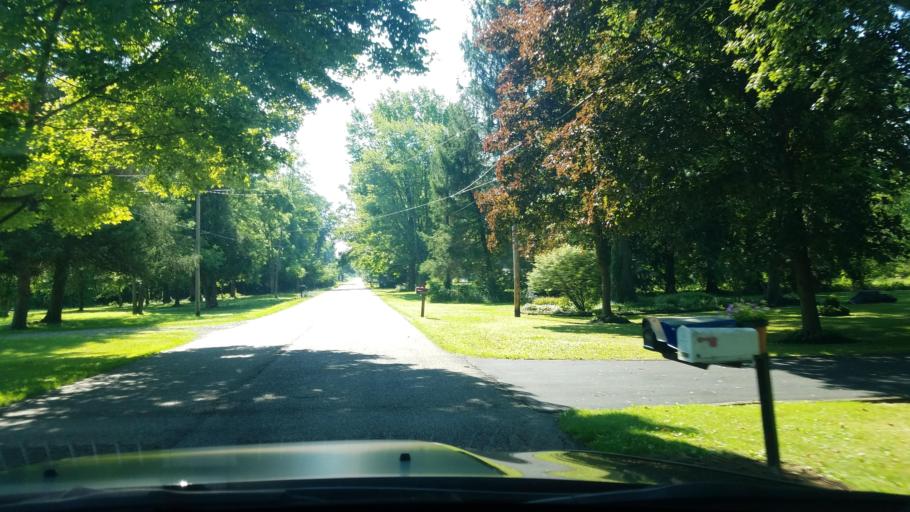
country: US
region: Ohio
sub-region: Trumbull County
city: Leavittsburg
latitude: 41.2577
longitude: -80.8989
